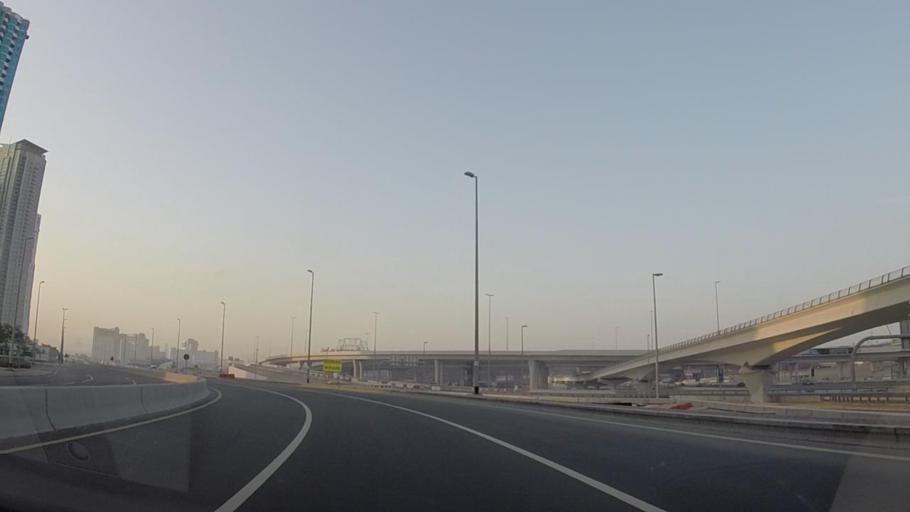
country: AE
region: Dubai
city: Dubai
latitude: 25.0680
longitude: 55.1369
